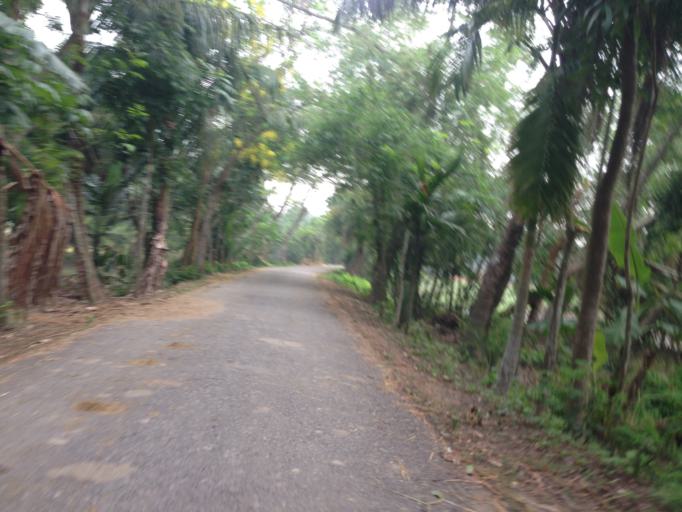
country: BD
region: Khulna
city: Kalia
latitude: 23.0425
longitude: 89.6450
